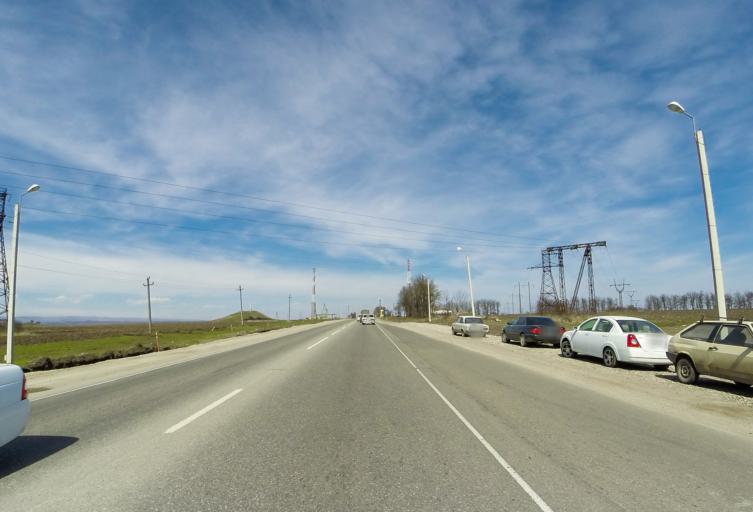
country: RU
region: Kabardino-Balkariya
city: Malka
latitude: 43.8070
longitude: 43.3640
